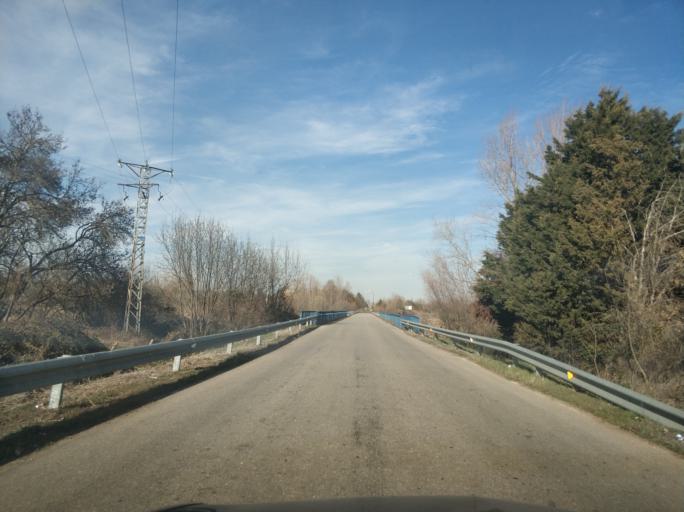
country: ES
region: Castille and Leon
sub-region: Provincia de Salamanca
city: Villamayor
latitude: 40.9912
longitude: -5.7285
